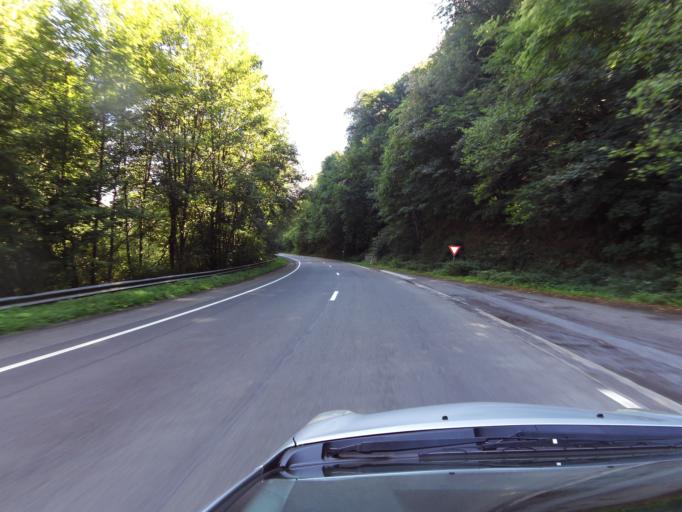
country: BE
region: Wallonia
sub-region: Province du Luxembourg
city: Rendeux
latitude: 50.2074
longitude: 5.5238
